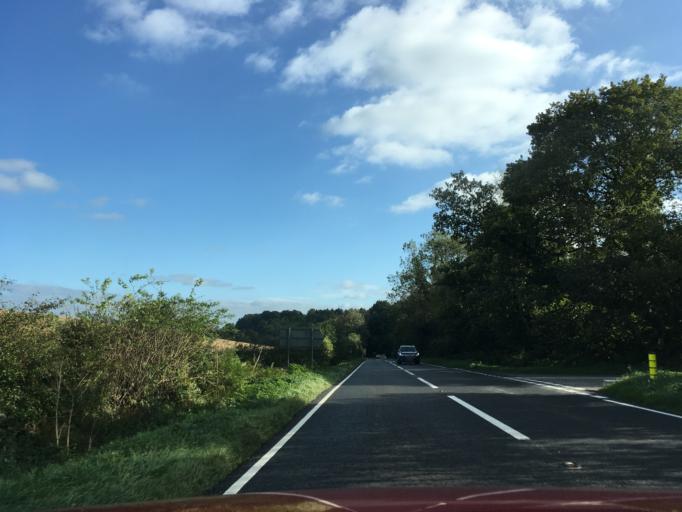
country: GB
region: England
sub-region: Hampshire
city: Four Marks
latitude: 51.1775
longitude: -1.0566
